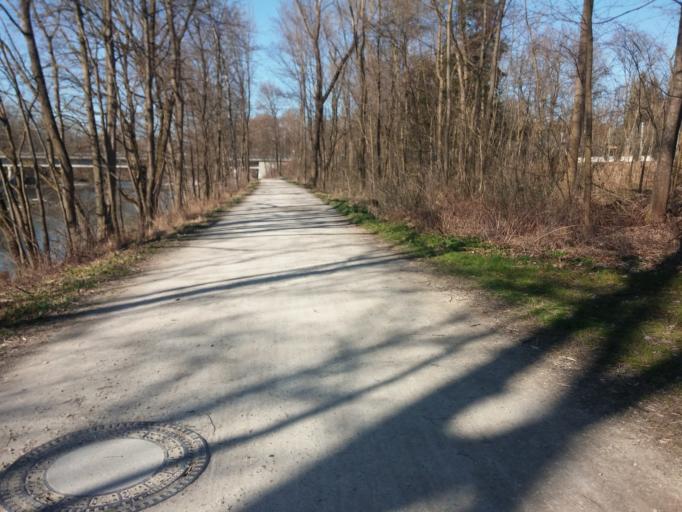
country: DE
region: Bavaria
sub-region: Upper Bavaria
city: Ismaning
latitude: 48.2366
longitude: 11.6731
